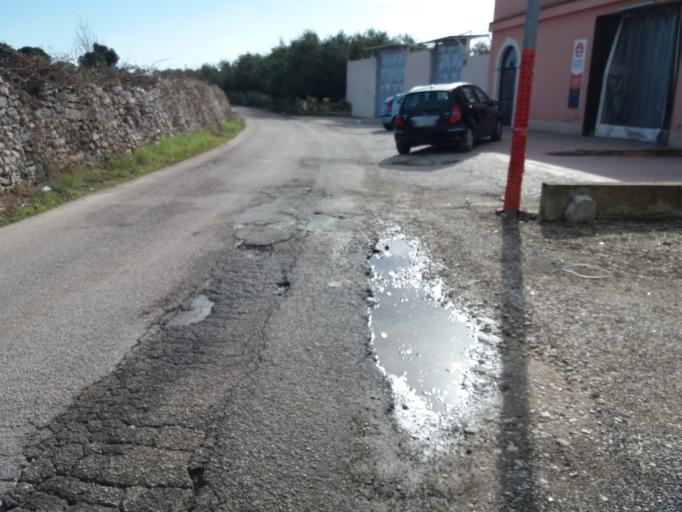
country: IT
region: Apulia
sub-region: Provincia di Barletta - Andria - Trani
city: Andria
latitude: 41.2161
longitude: 16.3057
